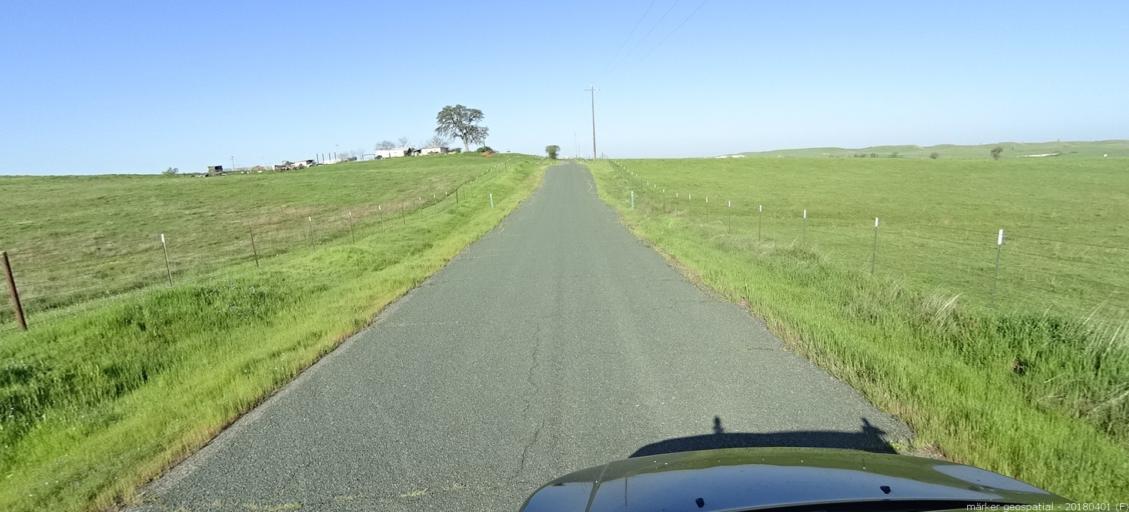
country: US
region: California
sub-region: Sacramento County
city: Rancho Murieta
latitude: 38.4641
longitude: -121.0405
